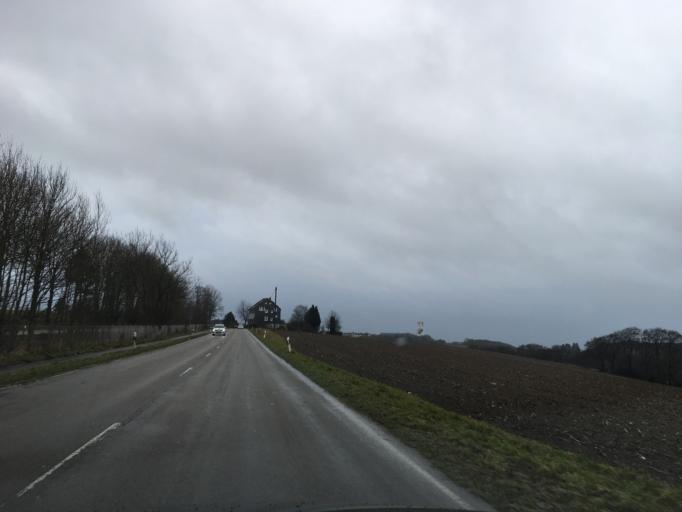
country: DE
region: North Rhine-Westphalia
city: Wulfrath
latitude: 51.3058
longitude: 7.0653
